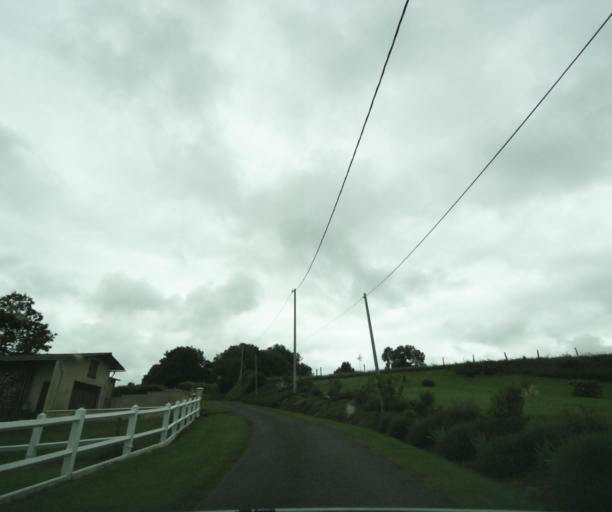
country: FR
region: Bourgogne
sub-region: Departement de Saone-et-Loire
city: Charolles
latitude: 46.4709
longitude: 4.3300
